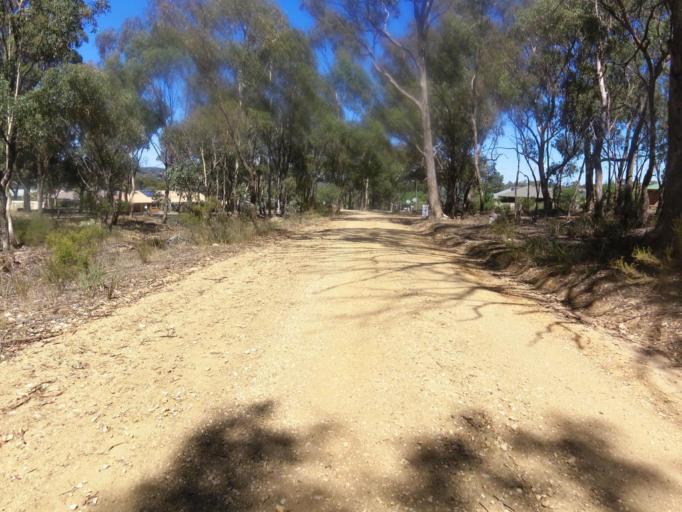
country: AU
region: Victoria
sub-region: Mount Alexander
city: Castlemaine
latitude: -37.0659
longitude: 144.1940
